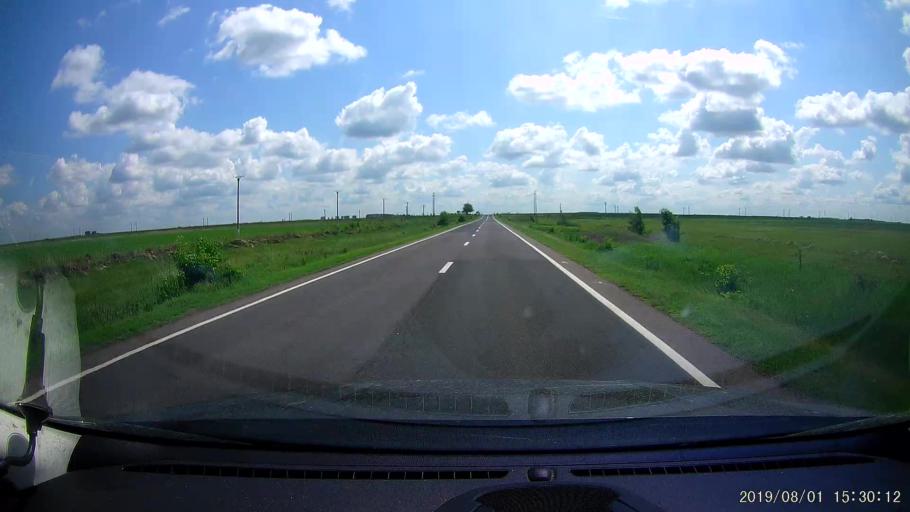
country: RO
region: Braila
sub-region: Comuna Viziru
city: Viziru
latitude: 44.9675
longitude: 27.6817
